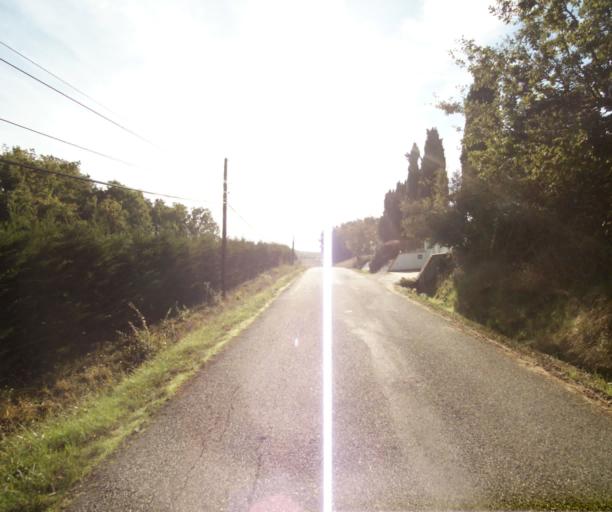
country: FR
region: Midi-Pyrenees
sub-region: Departement du Tarn-et-Garonne
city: Nohic
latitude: 43.9046
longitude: 1.4664
